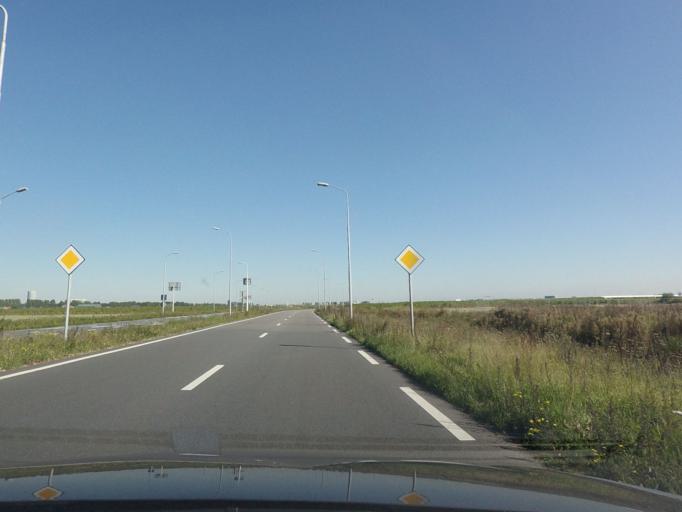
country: NL
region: North Holland
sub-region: Gemeente Haarlemmermeer
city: Hoofddorp
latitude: 52.2704
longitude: 4.6919
